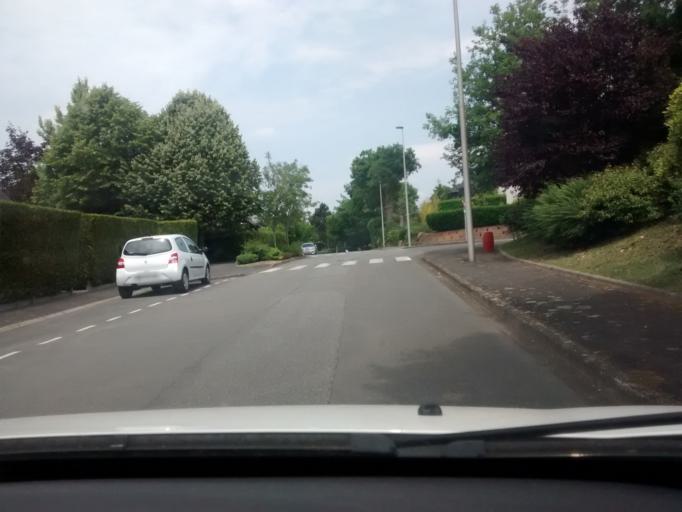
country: FR
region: Brittany
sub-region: Departement d'Ille-et-Vilaine
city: Cesson-Sevigne
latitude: 48.1251
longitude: -1.6049
